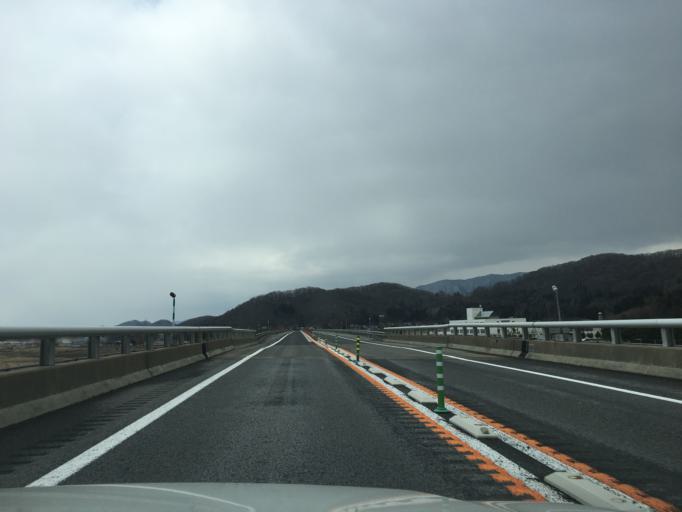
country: JP
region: Aomori
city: Aomori Shi
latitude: 40.8094
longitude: 140.8011
